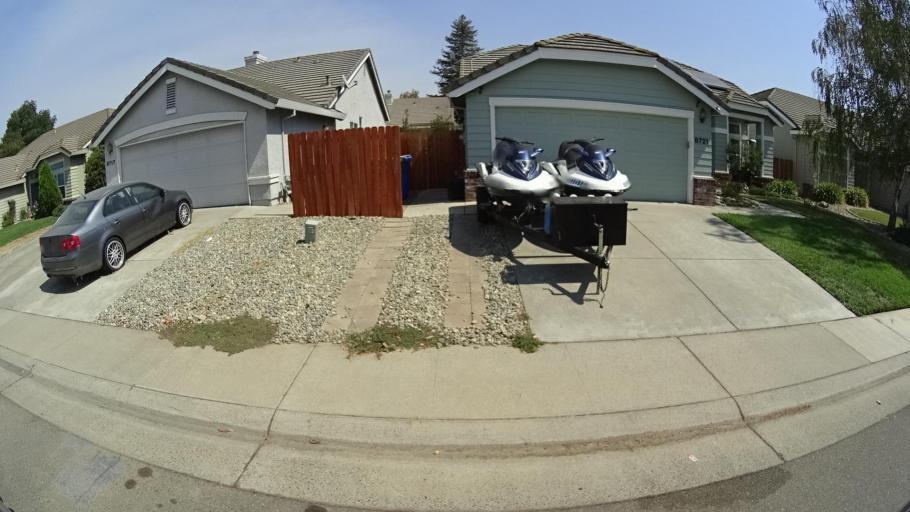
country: US
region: California
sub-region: Sacramento County
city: Elk Grove
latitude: 38.4427
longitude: -121.3741
